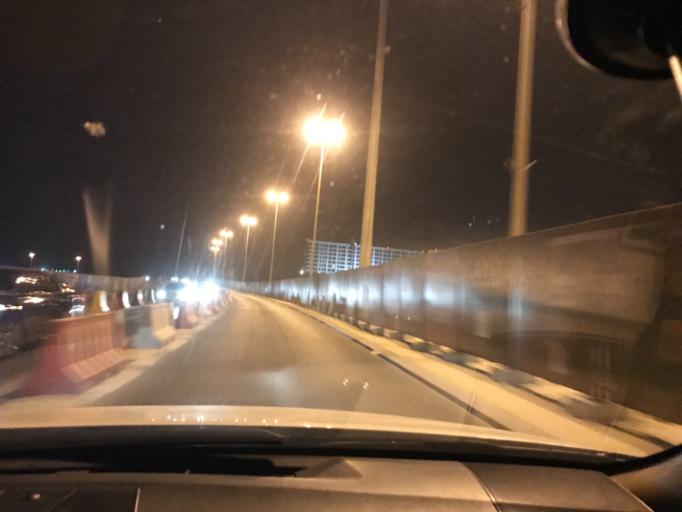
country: BH
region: Muharraq
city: Al Muharraq
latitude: 26.3006
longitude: 50.6428
